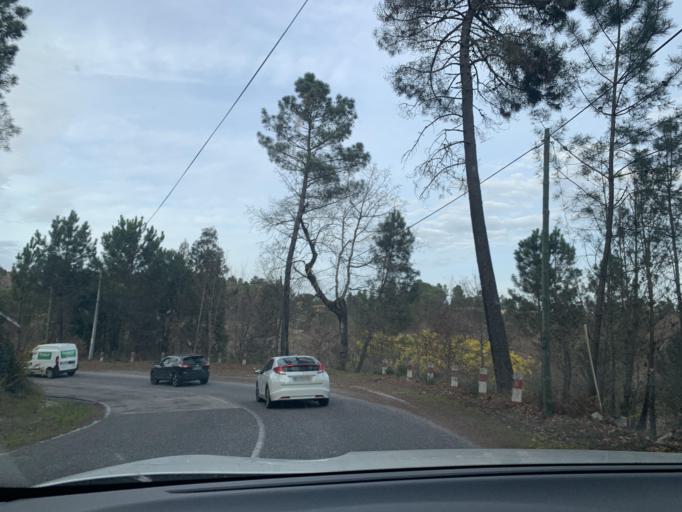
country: PT
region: Viseu
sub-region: Viseu
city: Viseu
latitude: 40.5989
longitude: -7.9919
